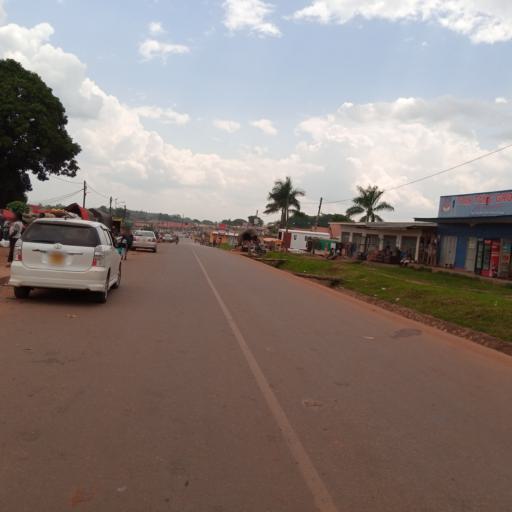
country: UG
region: Eastern Region
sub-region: Mbale District
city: Mbale
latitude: 1.0753
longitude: 34.1665
